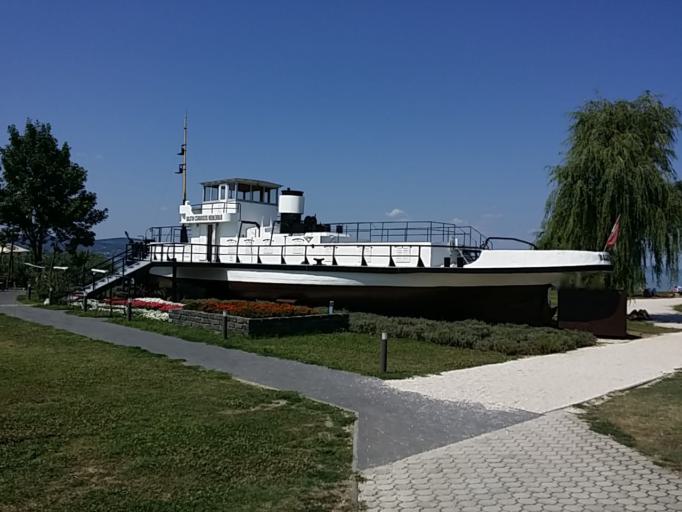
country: HU
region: Somogy
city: Balatonboglar
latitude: 46.7812
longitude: 17.6481
